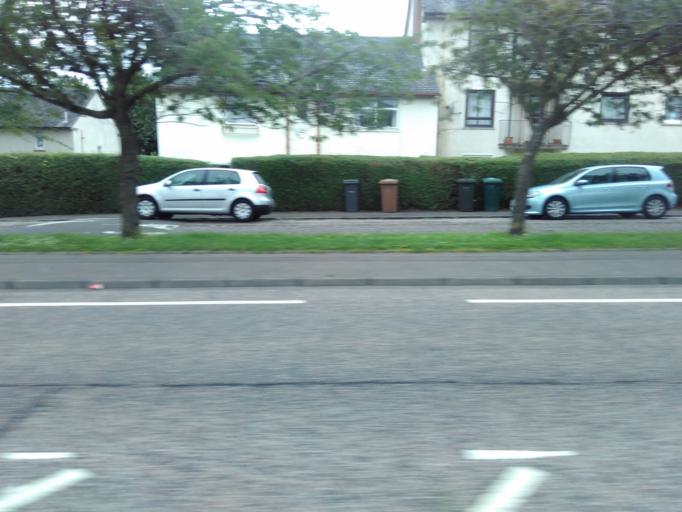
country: GB
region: Scotland
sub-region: Midlothian
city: Loanhead
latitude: 55.9183
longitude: -3.1548
